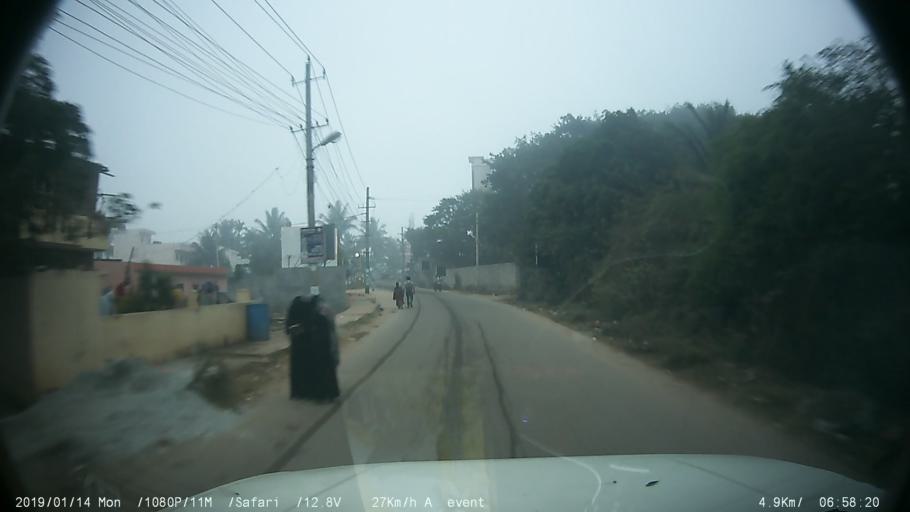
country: IN
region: Karnataka
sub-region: Bangalore Urban
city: Anekal
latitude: 12.8312
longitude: 77.6551
